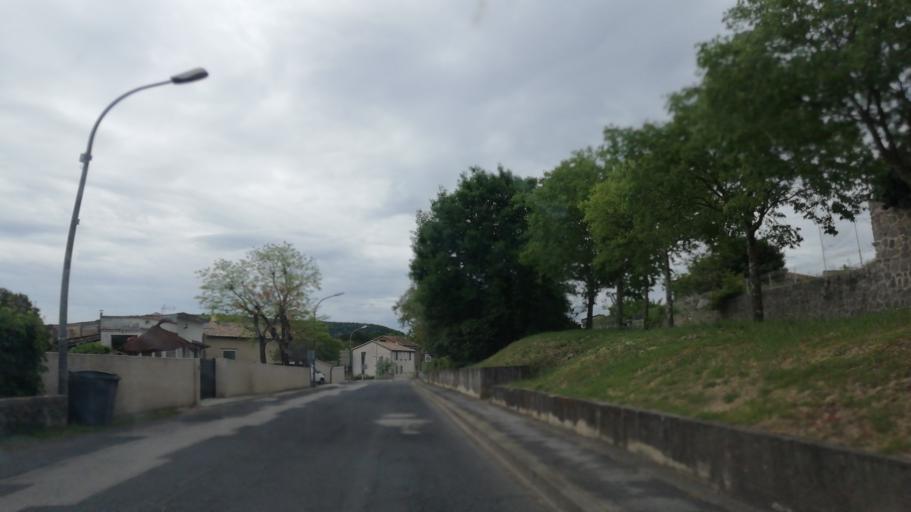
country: FR
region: Languedoc-Roussillon
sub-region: Departement de l'Herault
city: Saint-Martin-de-Londres
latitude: 43.7937
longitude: 3.7334
